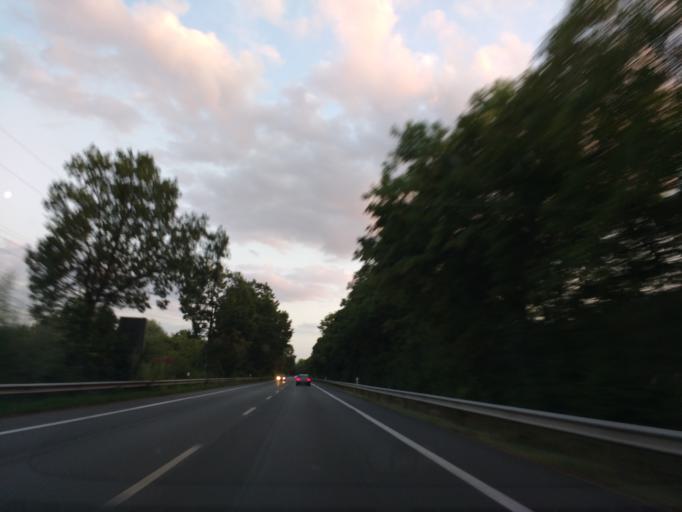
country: DE
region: North Rhine-Westphalia
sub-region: Regierungsbezirk Detmold
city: Petershagen
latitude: 52.3666
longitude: 8.9849
